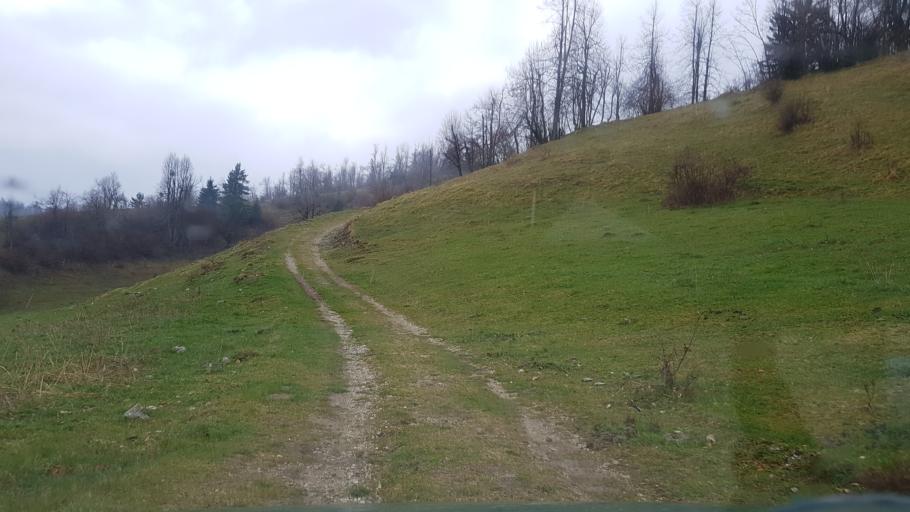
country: SI
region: Cerkno
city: Cerkno
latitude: 46.1422
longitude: 13.8689
